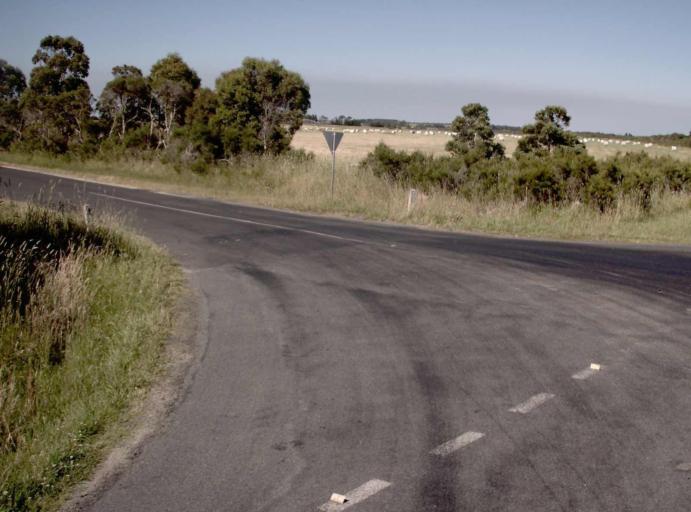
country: AU
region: Victoria
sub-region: Latrobe
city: Traralgon
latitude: -38.6348
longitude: 146.5828
